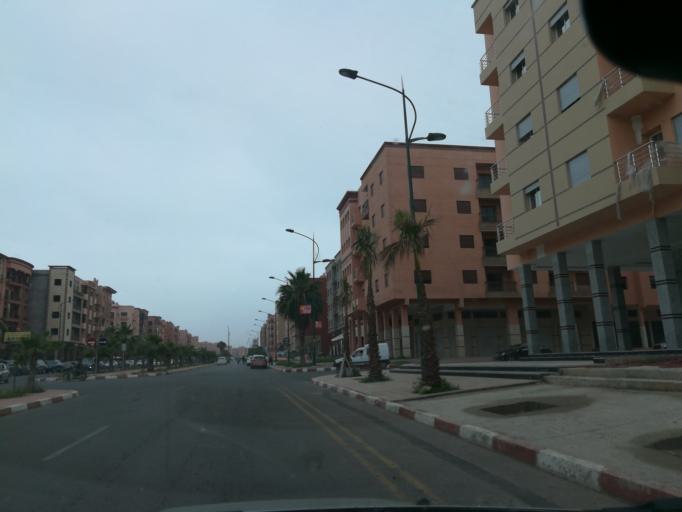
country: MA
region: Marrakech-Tensift-Al Haouz
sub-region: Marrakech
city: Marrakesh
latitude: 31.6736
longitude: -8.0220
